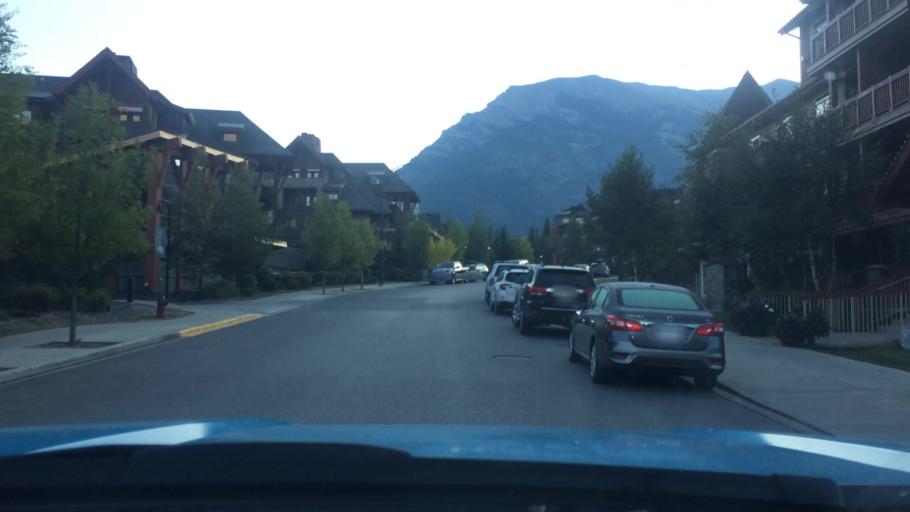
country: CA
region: Alberta
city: Canmore
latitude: 51.0828
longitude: -115.3423
